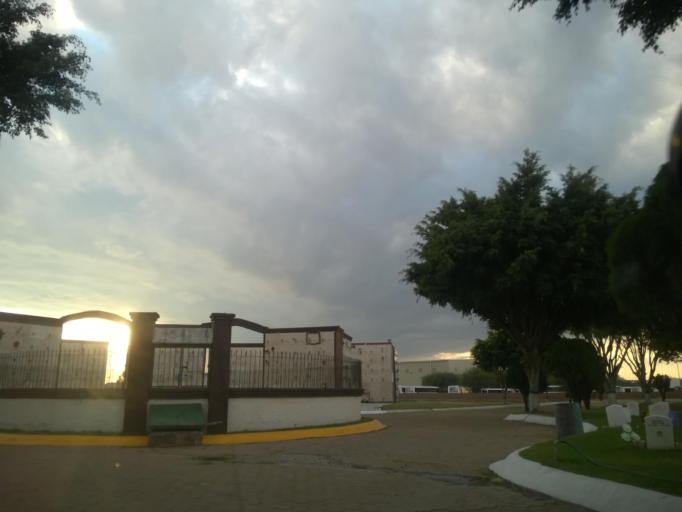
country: MX
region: Guanajuato
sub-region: Leon
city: Fraccionamiento Paraiso Real
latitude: 21.0934
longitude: -101.6189
